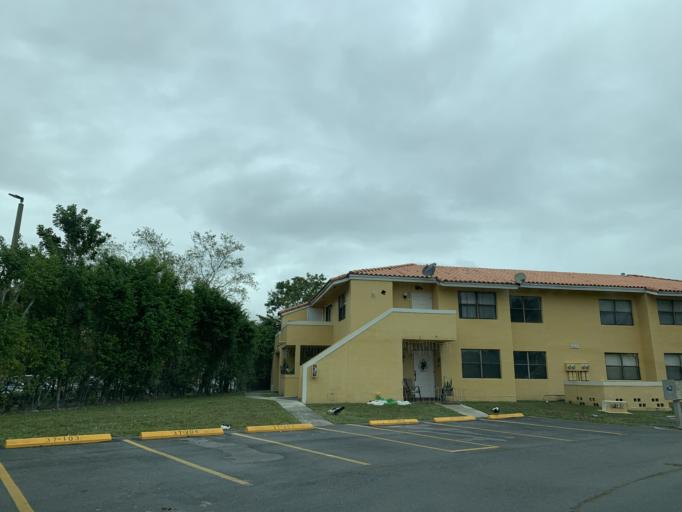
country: US
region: Florida
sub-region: Miami-Dade County
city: Kendall West
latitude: 25.6934
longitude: -80.4338
